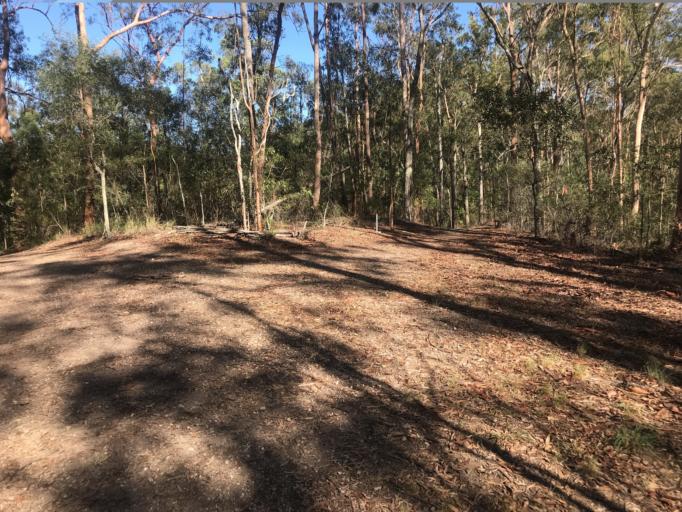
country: AU
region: Queensland
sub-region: Moreton Bay
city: Ferny Hills
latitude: -27.4405
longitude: 152.9157
